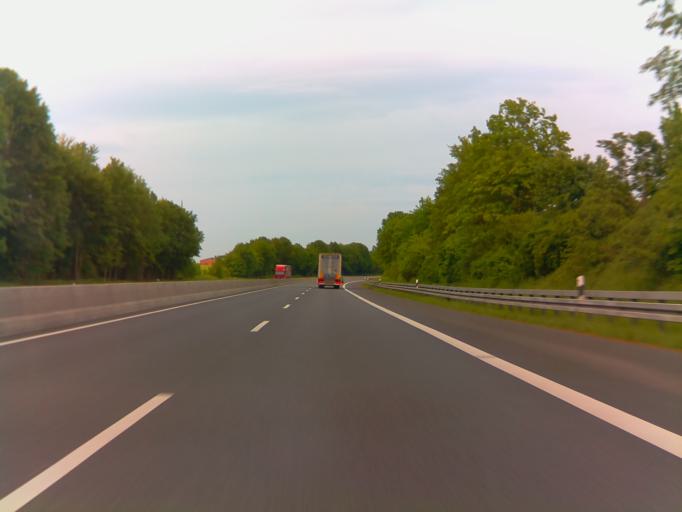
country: DE
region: Hesse
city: Gudensberg
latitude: 51.1676
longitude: 9.3231
